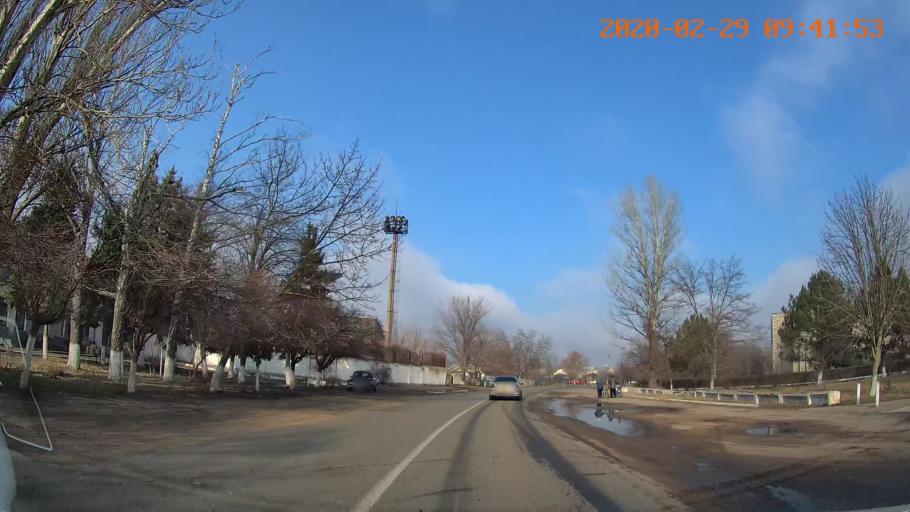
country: MD
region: Telenesti
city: Crasnoe
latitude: 46.6378
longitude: 29.8265
